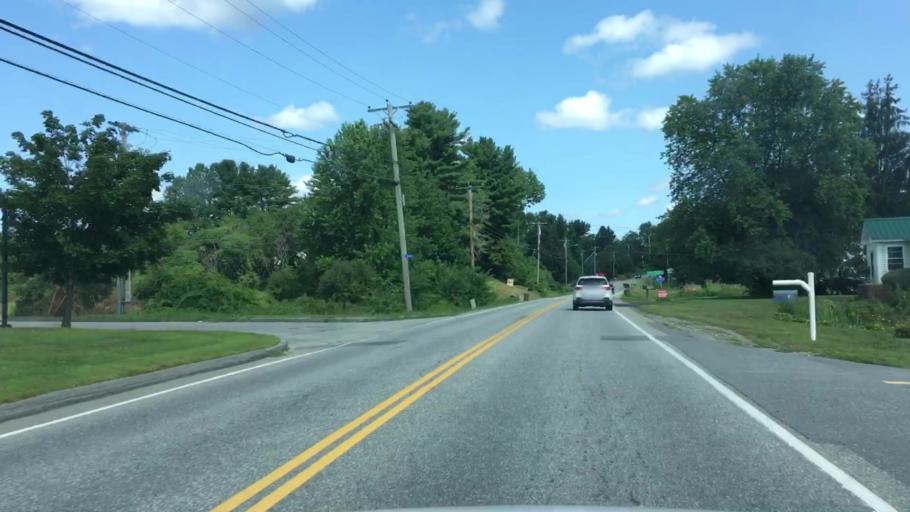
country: US
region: Maine
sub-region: Kennebec County
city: Augusta
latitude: 44.3271
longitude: -69.8178
